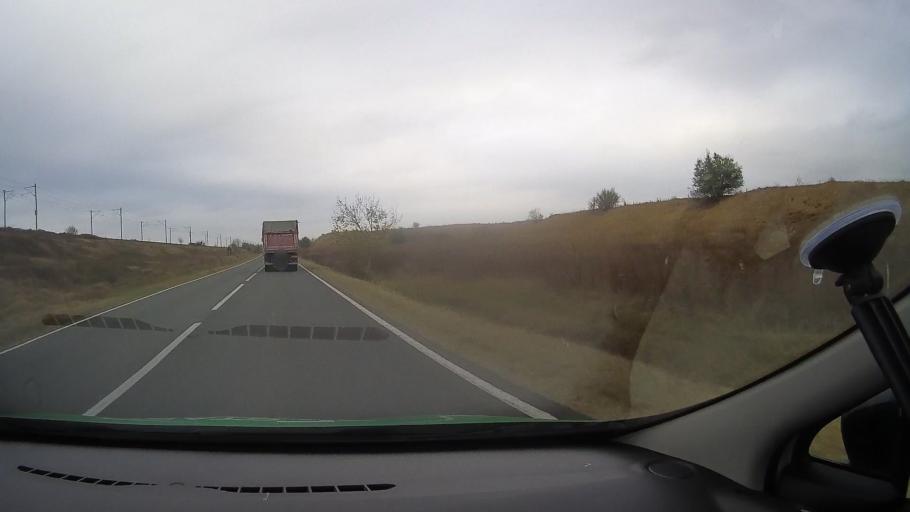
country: RO
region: Constanta
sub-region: Comuna Poarta Alba
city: Poarta Alba
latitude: 44.2227
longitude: 28.3862
